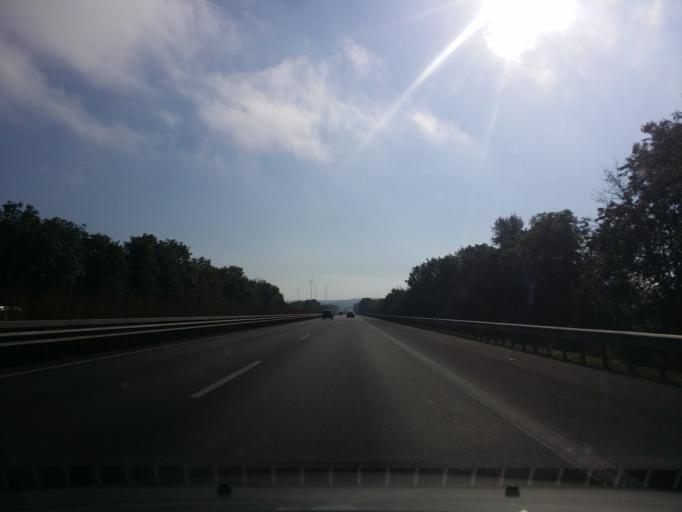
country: DE
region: Rheinland-Pfalz
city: Gundheim
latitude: 49.6794
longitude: 8.2535
